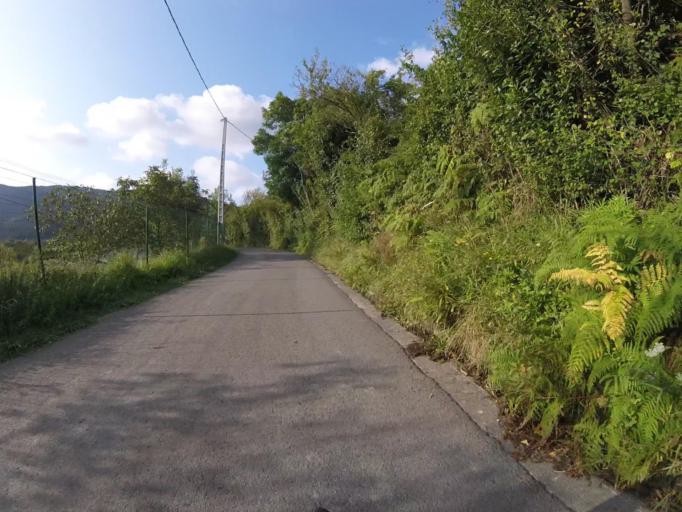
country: ES
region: Basque Country
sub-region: Provincia de Guipuzcoa
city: Fuenterrabia
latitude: 43.3485
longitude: -1.8196
